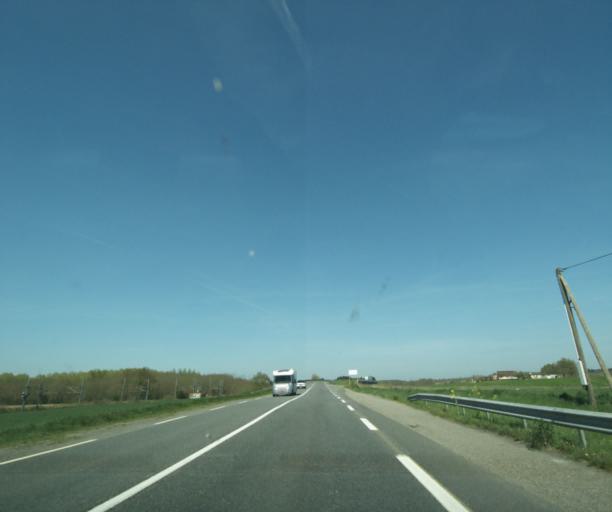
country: FR
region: Bourgogne
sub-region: Departement de la Nievre
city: Chantenay-Saint-Imbert
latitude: 46.6726
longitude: 3.2357
